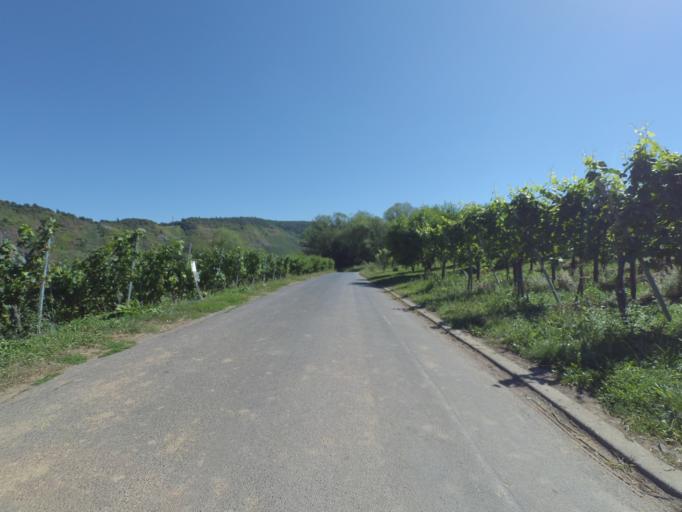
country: DE
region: Rheinland-Pfalz
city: Neef
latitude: 50.0947
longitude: 7.1281
